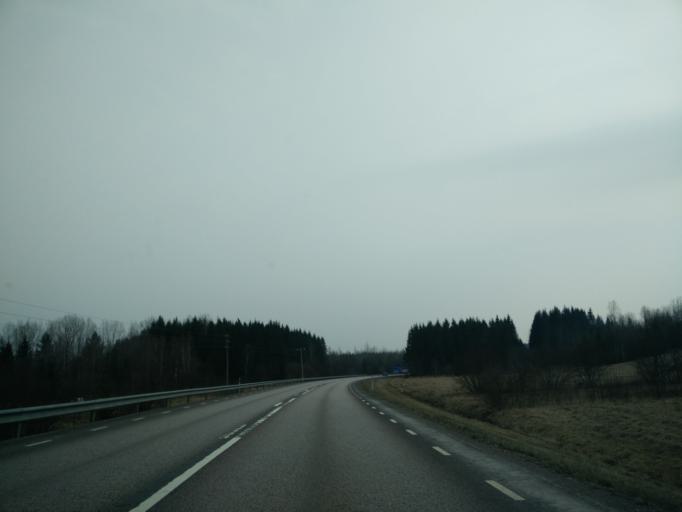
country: SE
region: Vaermland
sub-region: Forshaga Kommun
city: Forshaga
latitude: 59.5593
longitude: 13.4821
